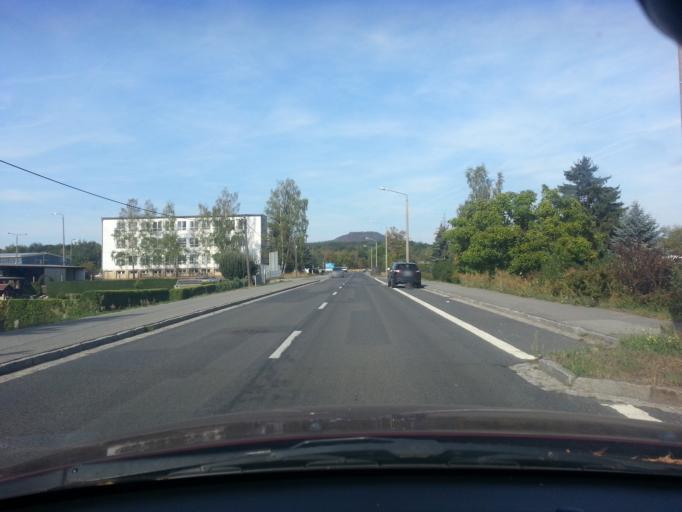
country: DE
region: Saxony
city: Goerlitz
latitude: 51.1166
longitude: 14.9744
